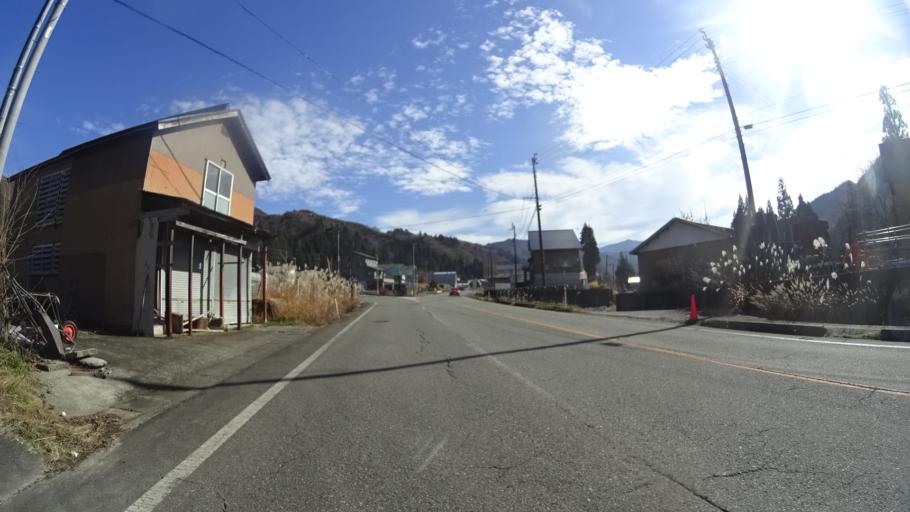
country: JP
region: Niigata
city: Muikamachi
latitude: 37.2050
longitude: 139.0709
